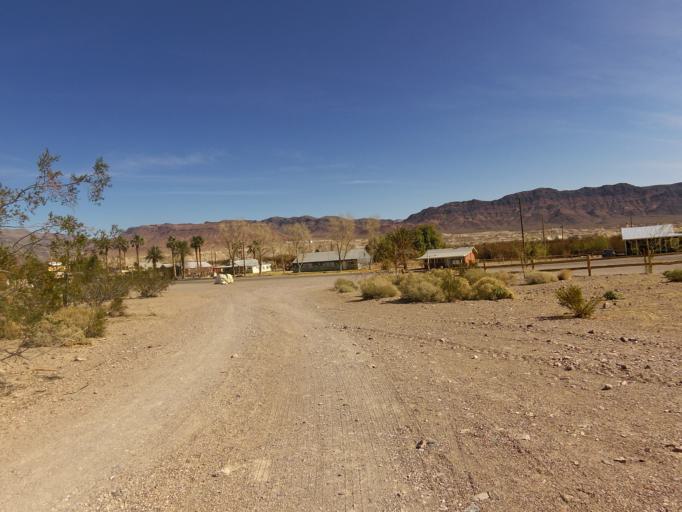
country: US
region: Nevada
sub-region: Nye County
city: Pahrump
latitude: 35.9735
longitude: -116.2710
